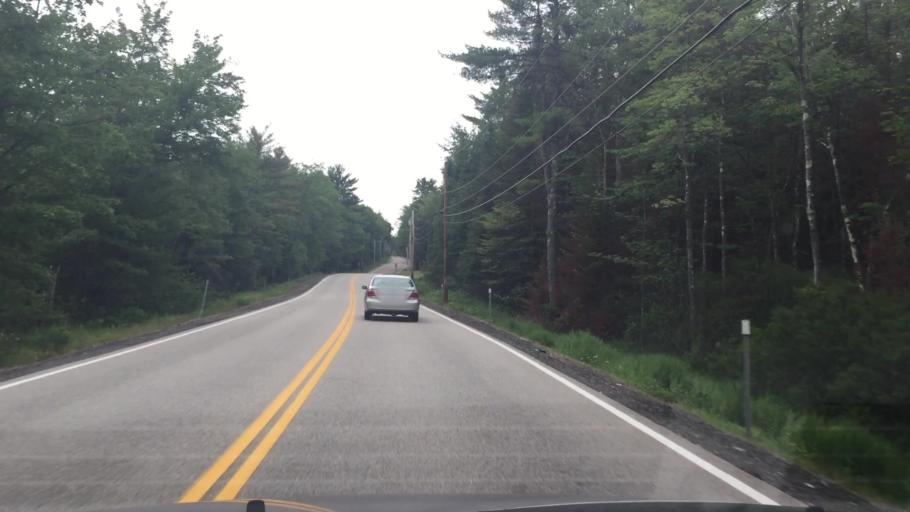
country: US
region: New Hampshire
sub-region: Carroll County
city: Conway
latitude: 43.9649
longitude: -71.1080
